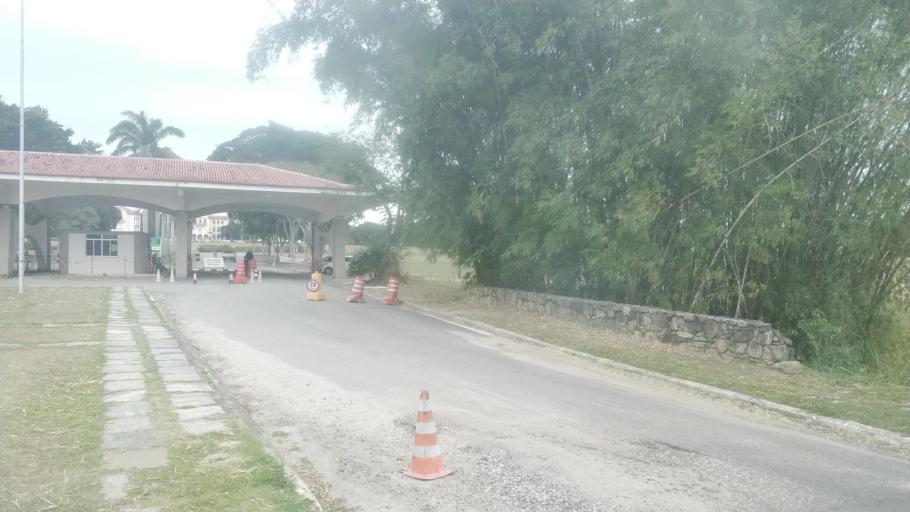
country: BR
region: Rio de Janeiro
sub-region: Seropedica
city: Seropedica
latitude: -22.7613
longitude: -43.6867
